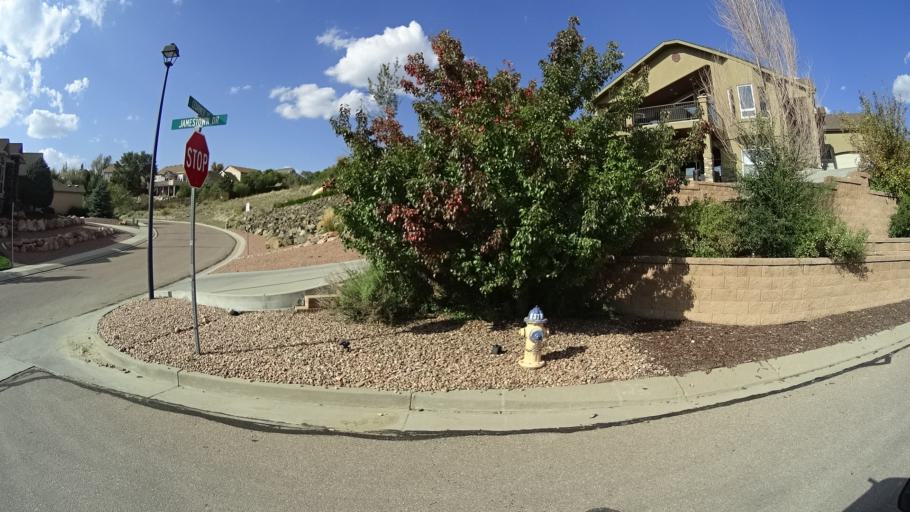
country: US
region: Colorado
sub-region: El Paso County
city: Cimarron Hills
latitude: 38.9125
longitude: -104.7379
